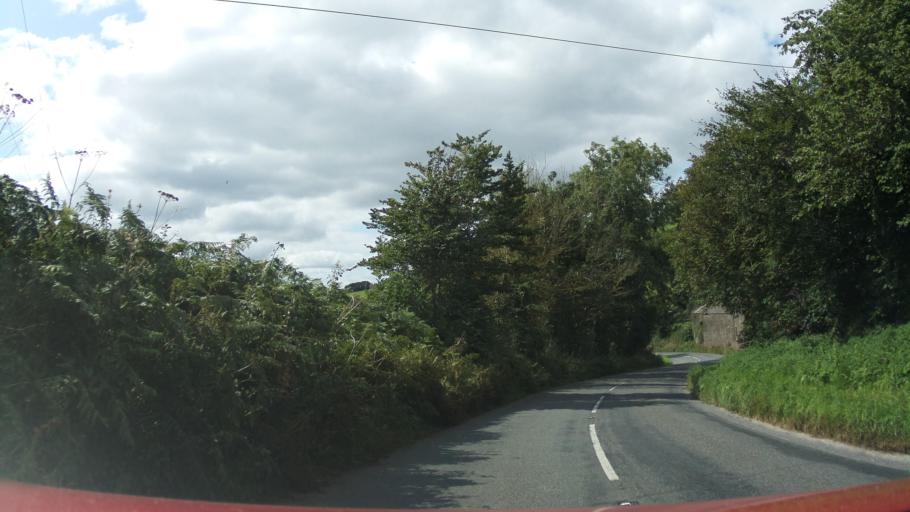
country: GB
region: England
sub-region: Devon
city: Dartmouth
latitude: 50.3639
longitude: -3.5533
